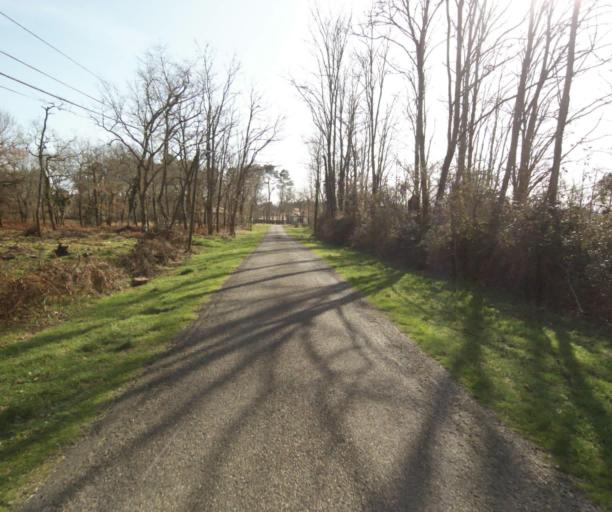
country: FR
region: Aquitaine
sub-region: Departement des Landes
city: Roquefort
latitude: 44.1263
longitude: -0.1920
